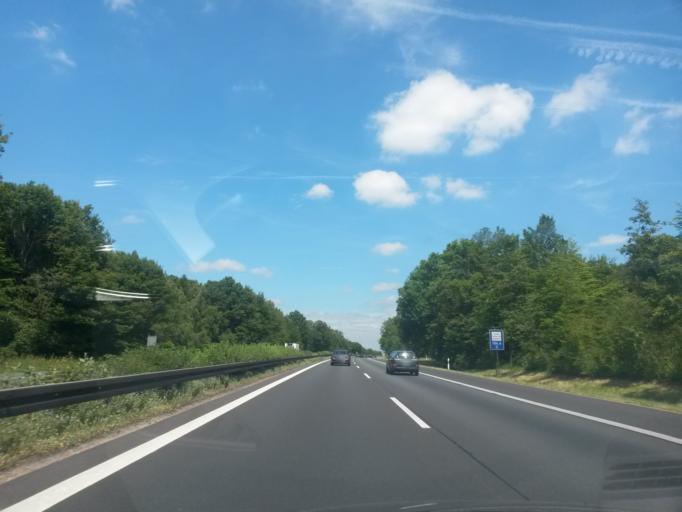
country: DE
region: Bavaria
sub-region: Regierungsbezirk Unterfranken
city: Arnstein
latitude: 49.9265
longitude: 9.9981
